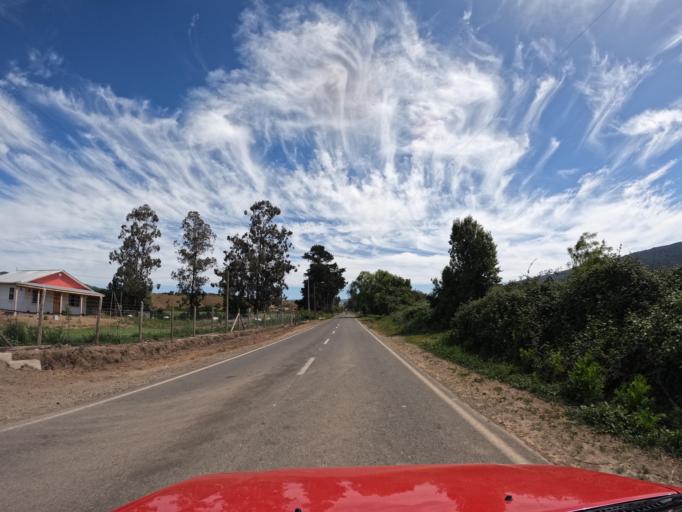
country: CL
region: Maule
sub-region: Provincia de Talca
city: Constitucion
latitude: -35.0024
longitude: -72.0261
